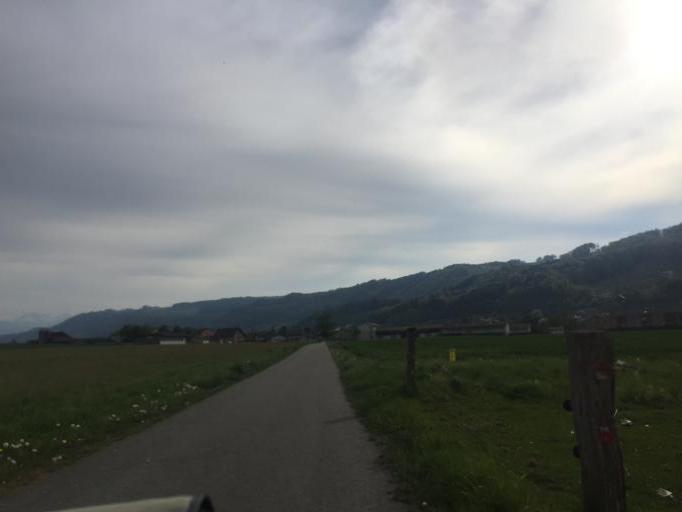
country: CH
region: Bern
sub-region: Bern-Mittelland District
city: Belp
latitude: 46.8875
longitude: 7.5073
